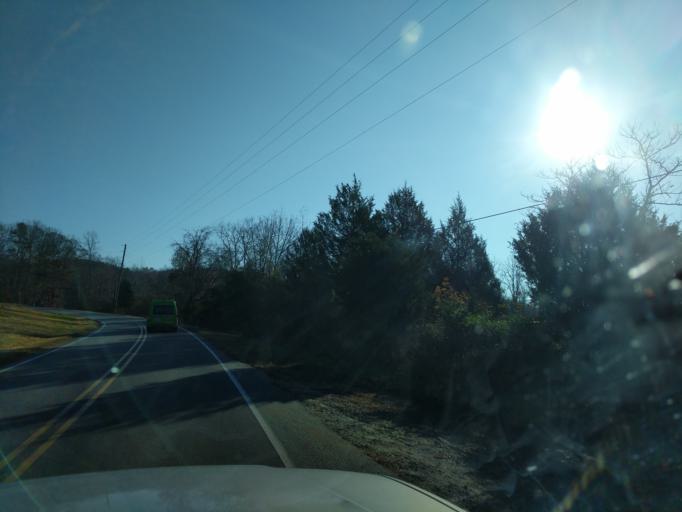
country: US
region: North Carolina
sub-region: Rutherford County
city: Rutherfordton
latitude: 35.2841
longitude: -82.0190
